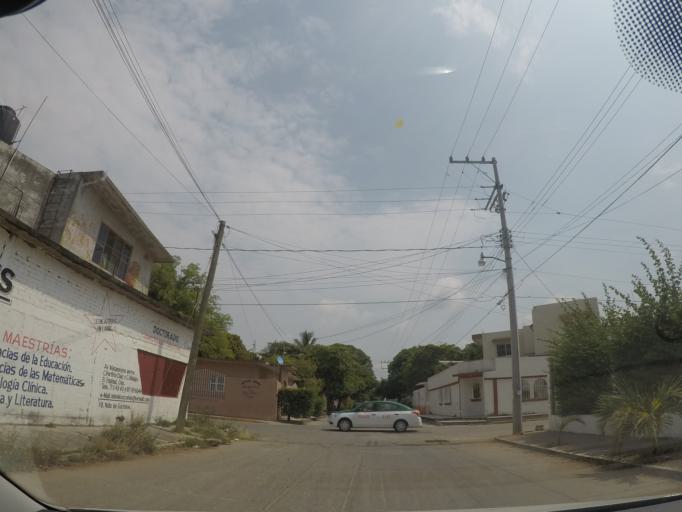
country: MX
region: Oaxaca
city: El Espinal
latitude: 16.4789
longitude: -95.0386
